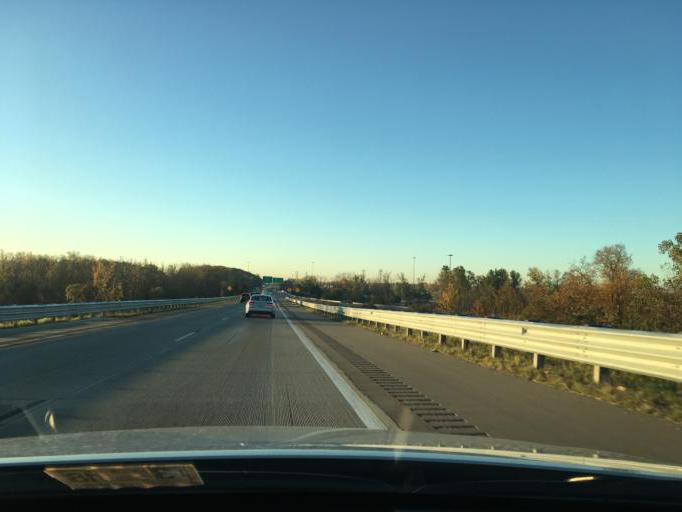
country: US
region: Michigan
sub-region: Oakland County
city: Novi
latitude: 42.4836
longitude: -83.4322
